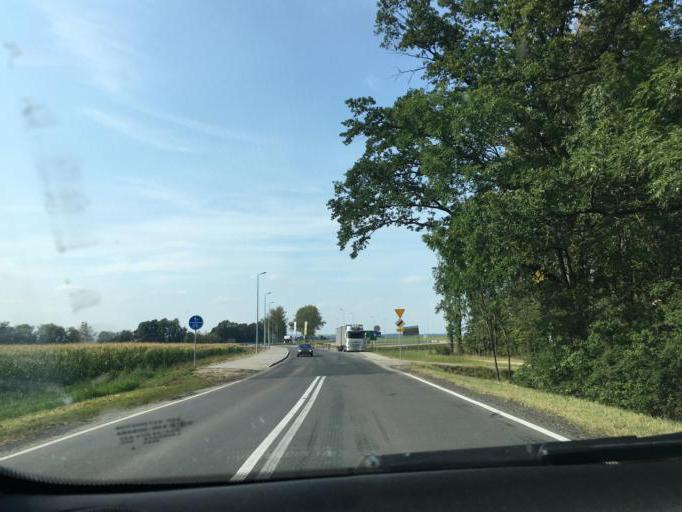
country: PL
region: Opole Voivodeship
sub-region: Powiat nyski
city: Nysa
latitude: 50.4393
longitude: 17.4062
